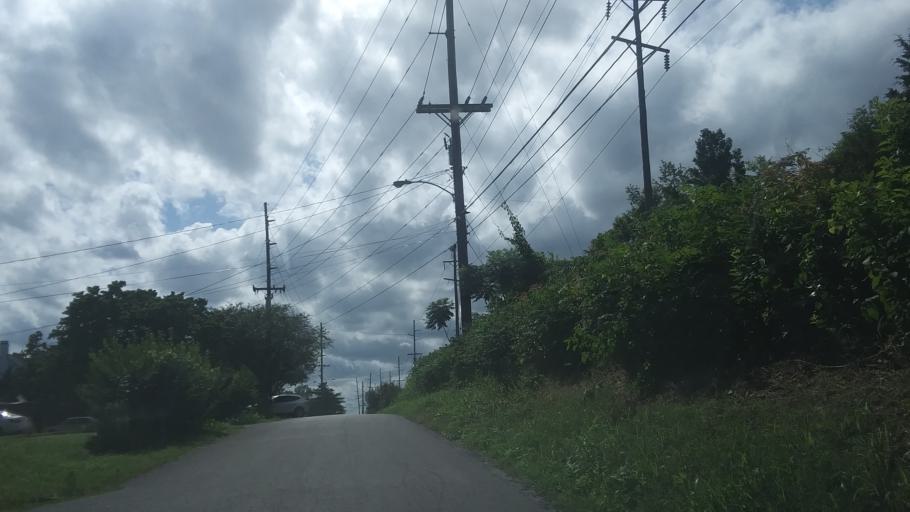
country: US
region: Tennessee
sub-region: Davidson County
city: Oak Hill
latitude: 36.0983
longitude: -86.6757
